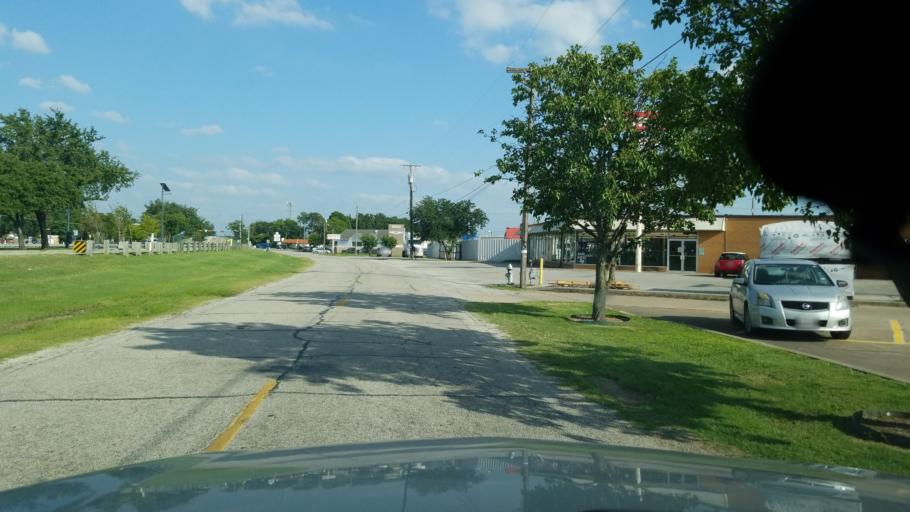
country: US
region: Texas
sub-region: Dallas County
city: Irving
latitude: 32.8194
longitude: -96.9654
